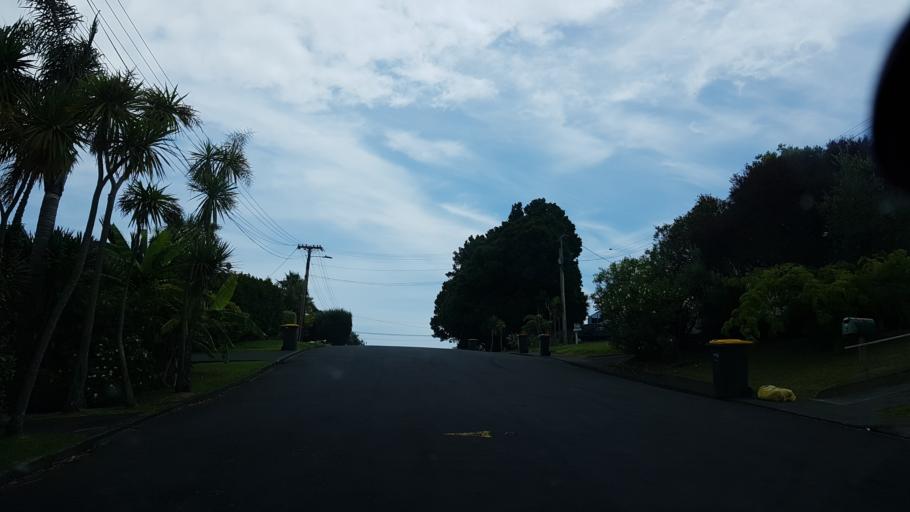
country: NZ
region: Auckland
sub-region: Auckland
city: North Shore
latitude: -36.8079
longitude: 174.7819
